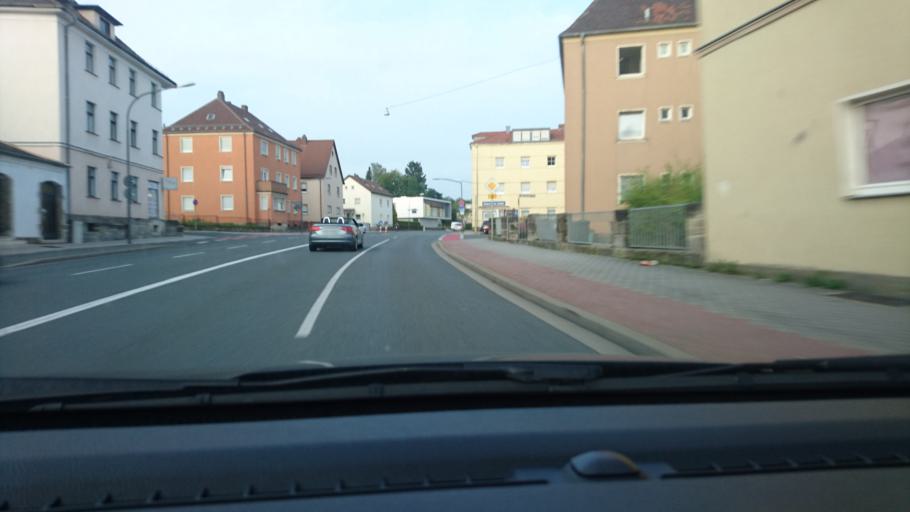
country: DE
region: Bavaria
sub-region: Upper Franconia
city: Bayreuth
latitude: 49.9481
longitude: 11.5889
